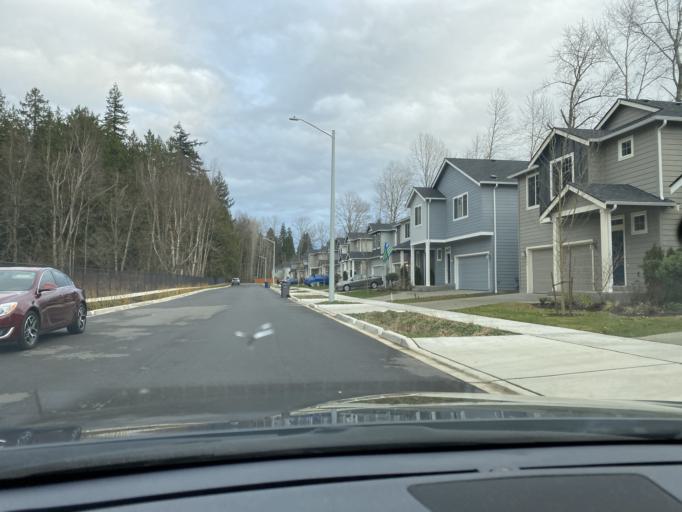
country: US
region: Washington
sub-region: Snohomish County
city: Marysville
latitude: 48.0818
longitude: -122.1548
